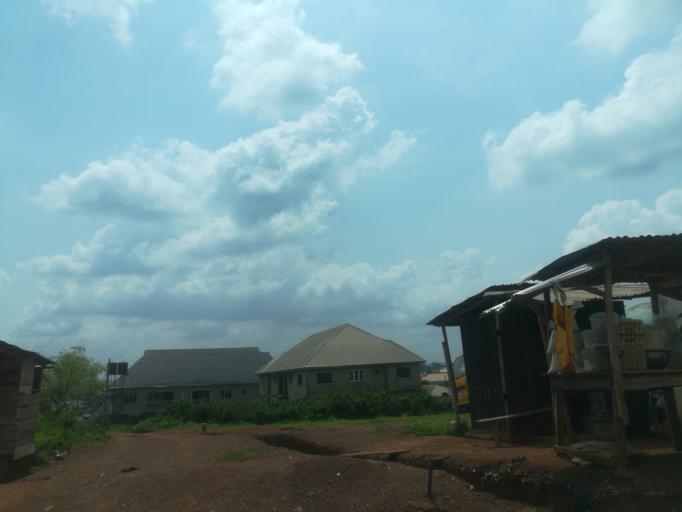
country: NG
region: Oyo
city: Moniya
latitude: 7.4678
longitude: 3.9576
